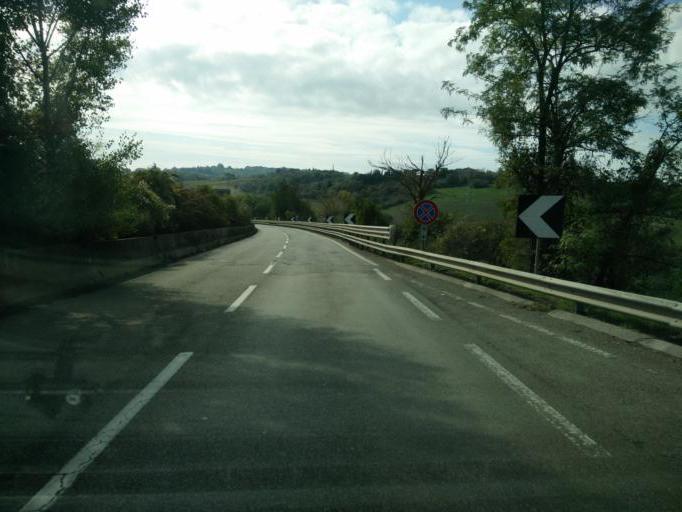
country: IT
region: Tuscany
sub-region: Provincia di Siena
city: Belverde
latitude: 43.3346
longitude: 11.2915
